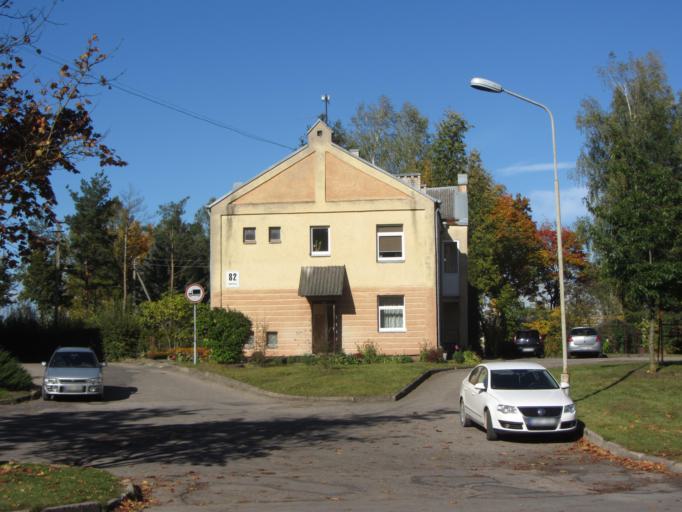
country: LT
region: Utenos apskritis
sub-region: Utena
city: Utena
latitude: 55.5102
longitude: 25.5990
